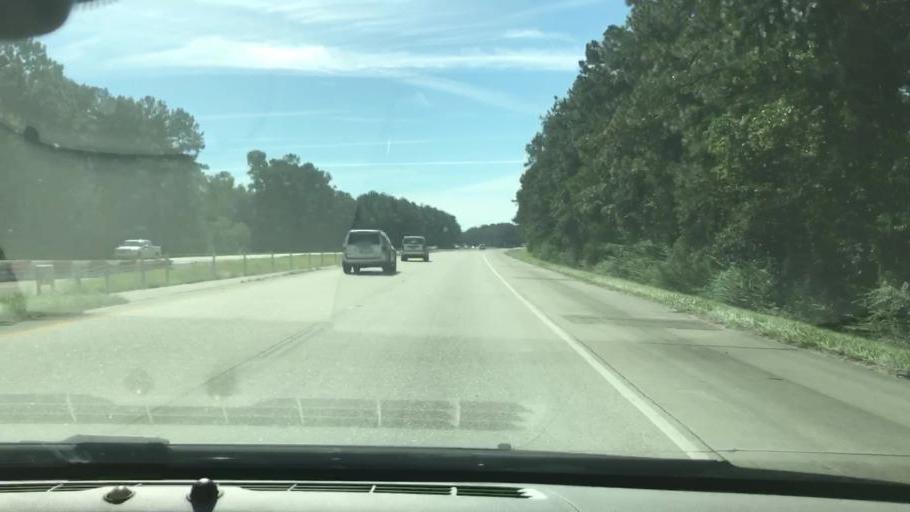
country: US
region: Louisiana
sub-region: Saint Tammany Parish
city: Slidell
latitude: 30.3156
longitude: -89.7385
